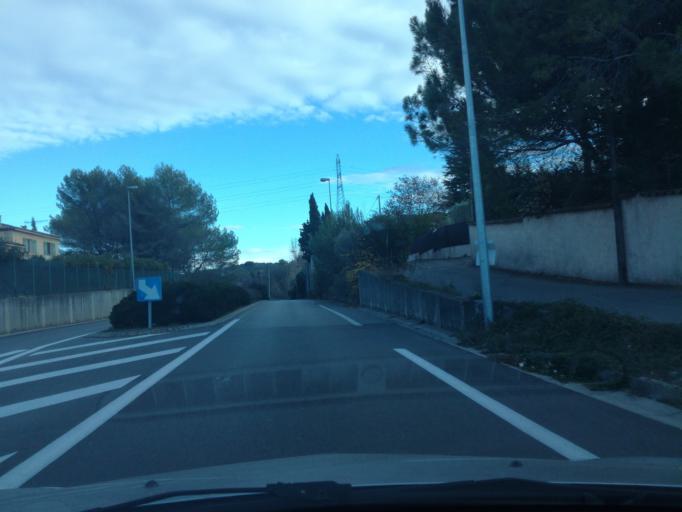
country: FR
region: Provence-Alpes-Cote d'Azur
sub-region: Departement des Alpes-Maritimes
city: Mougins
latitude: 43.6025
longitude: 7.0062
